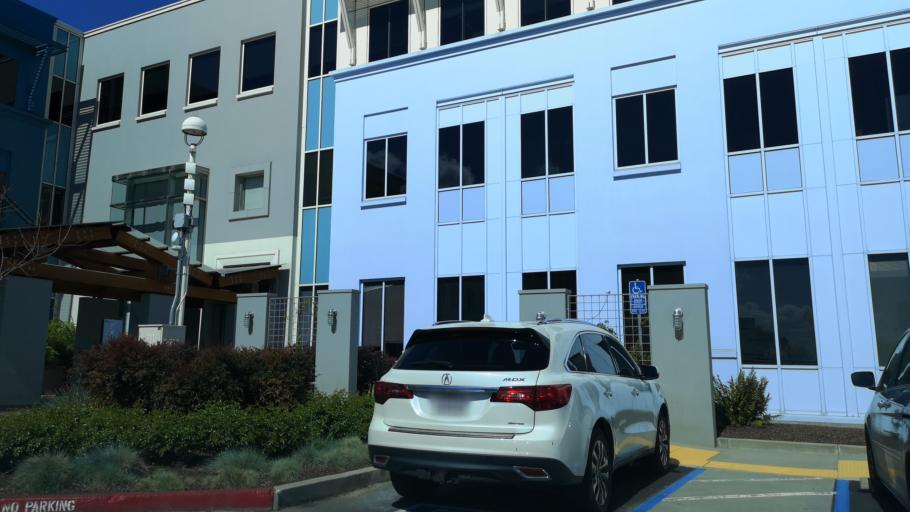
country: US
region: California
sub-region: San Mateo County
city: East Palo Alto
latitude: 37.4850
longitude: -122.1470
